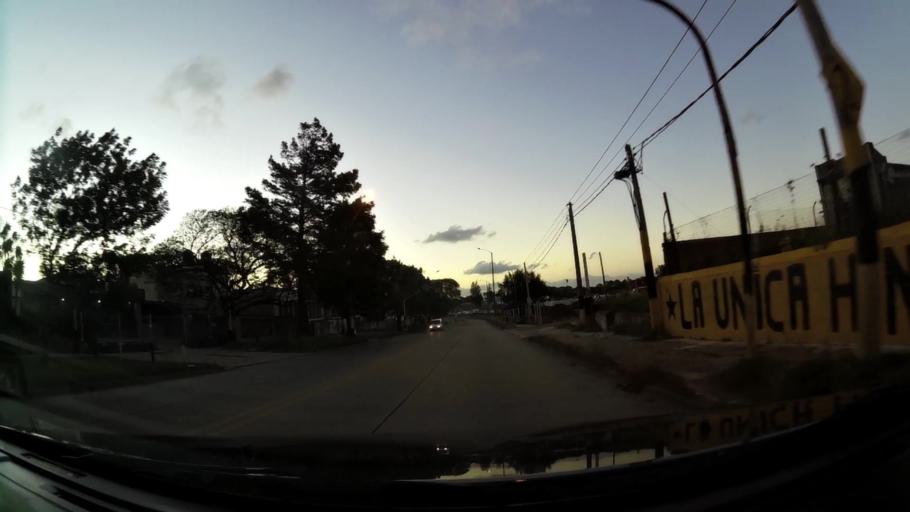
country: UY
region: Canelones
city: Paso de Carrasco
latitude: -34.8704
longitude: -56.1062
